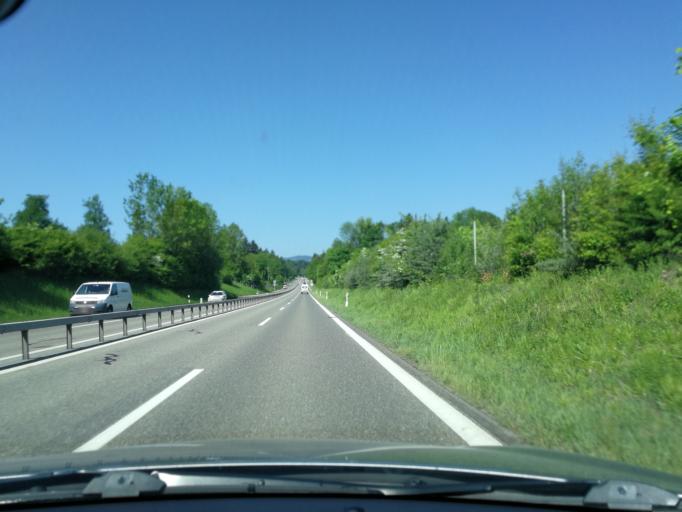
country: CH
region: Zurich
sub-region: Bezirk Hinwil
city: Binzikon
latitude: 47.2891
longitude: 8.7619
